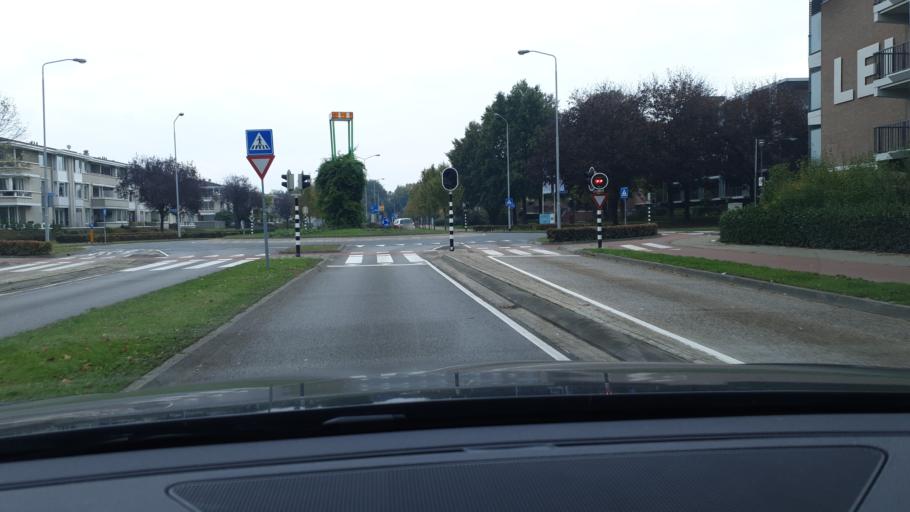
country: NL
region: North Brabant
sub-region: Gemeente Veldhoven
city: Veldhoven
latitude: 51.4216
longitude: 5.4080
